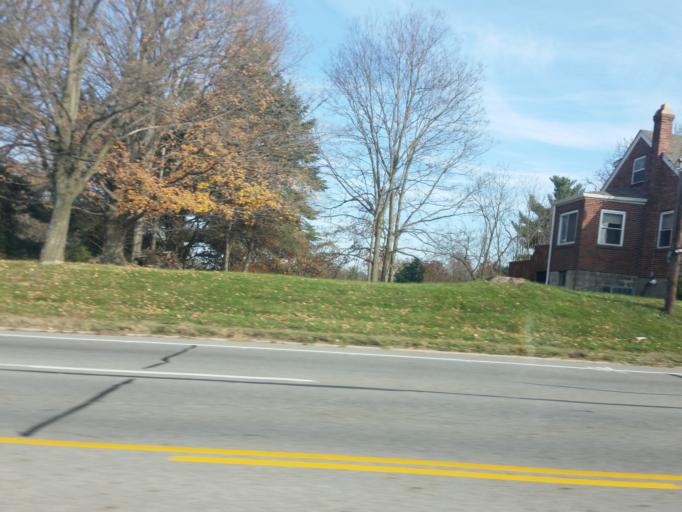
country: US
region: Kentucky
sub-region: Campbell County
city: Alexandria
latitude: 38.9764
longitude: -84.3927
